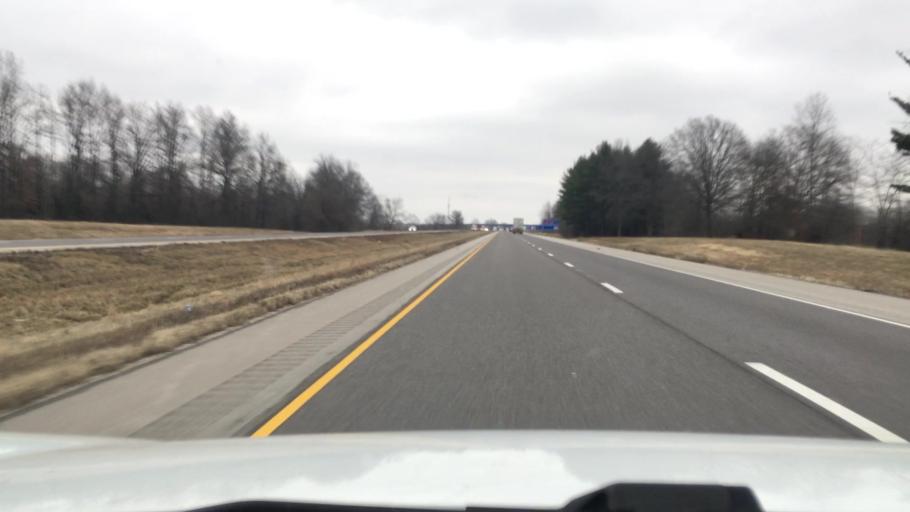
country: US
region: Illinois
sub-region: Effingham County
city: Altamont
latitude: 39.0357
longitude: -88.7767
